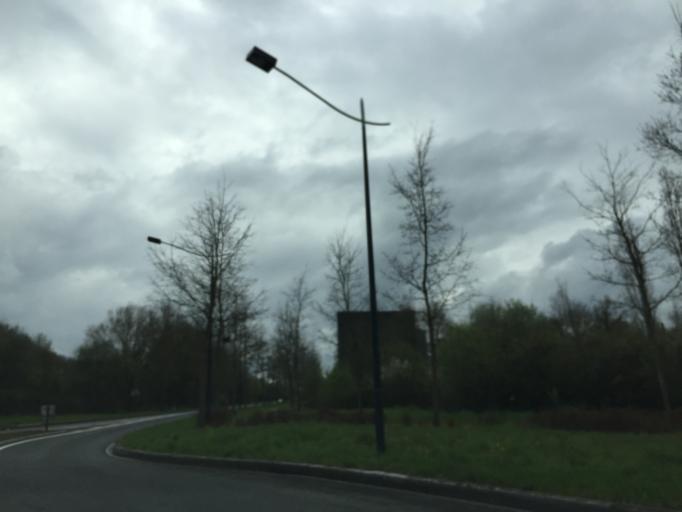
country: FR
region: Pays de la Loire
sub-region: Departement de la Loire-Atlantique
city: Carquefou
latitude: 47.2847
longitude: -1.5103
